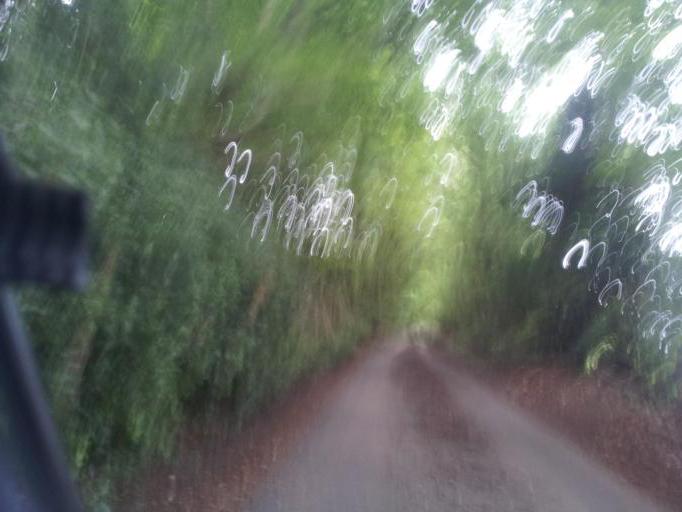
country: GB
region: England
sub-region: Kent
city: Newington
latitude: 51.3054
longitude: 0.6516
